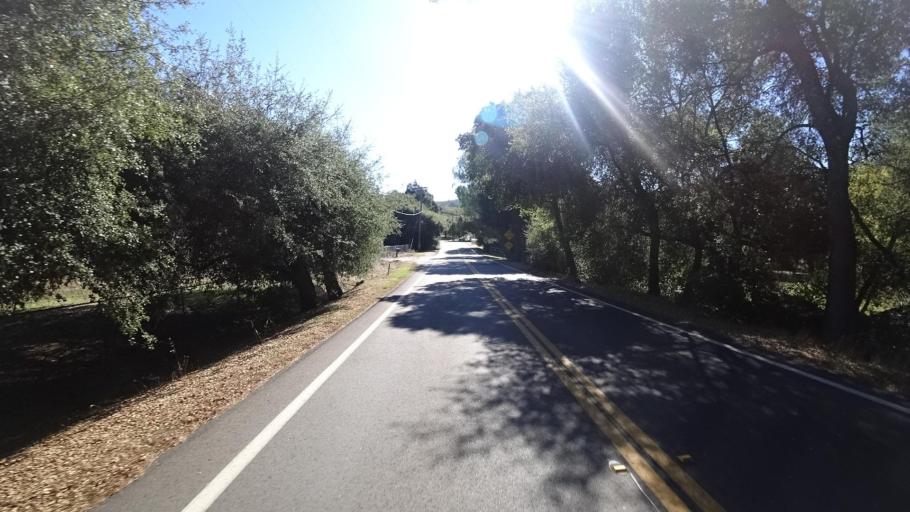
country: US
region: California
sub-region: San Diego County
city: Jamul
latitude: 32.6788
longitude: -116.7524
